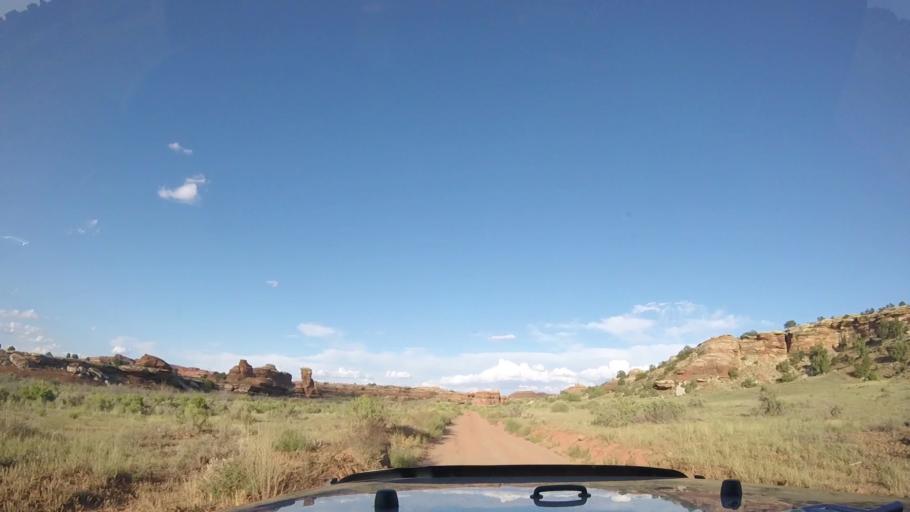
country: US
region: Utah
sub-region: Grand County
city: Moab
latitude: 38.1924
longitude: -109.7832
